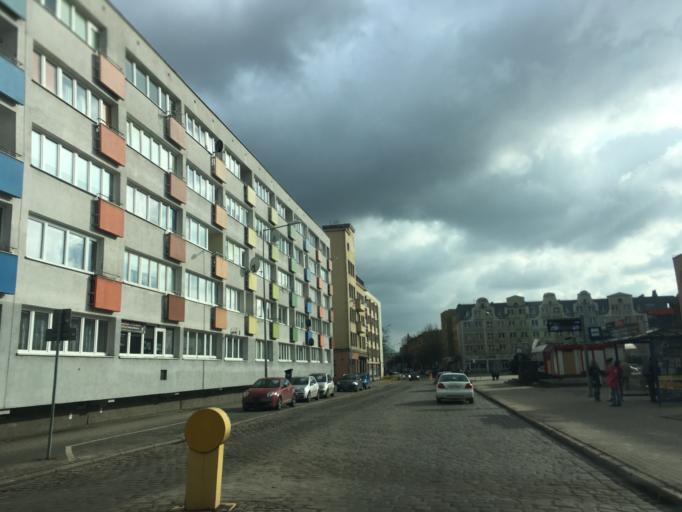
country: PL
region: Pomeranian Voivodeship
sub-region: Slupsk
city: Slupsk
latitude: 54.4678
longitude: 17.0311
